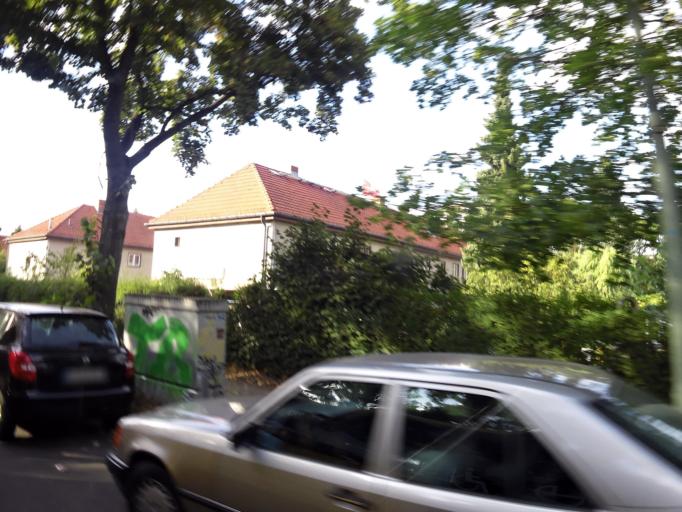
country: DE
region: Berlin
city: Marienfelde
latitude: 52.4262
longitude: 13.3692
